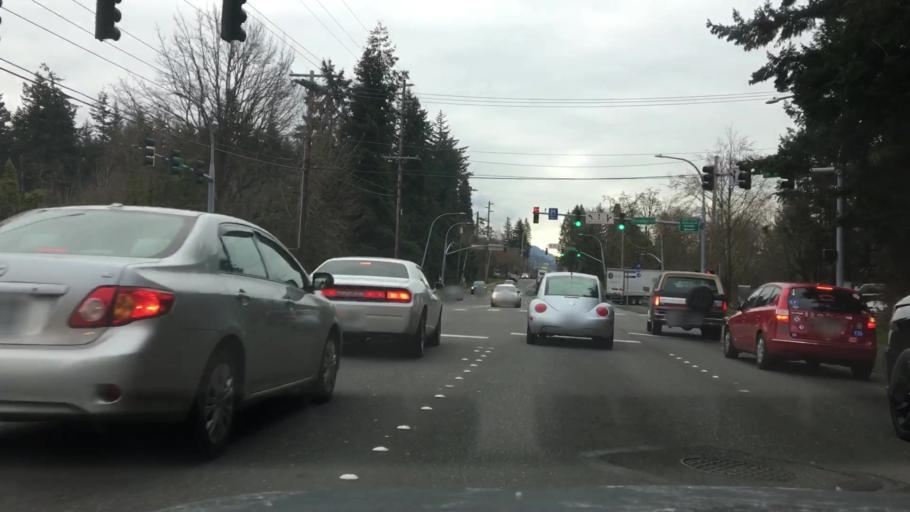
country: US
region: Washington
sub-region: Whatcom County
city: Bellingham
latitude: 48.7773
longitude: -122.4862
